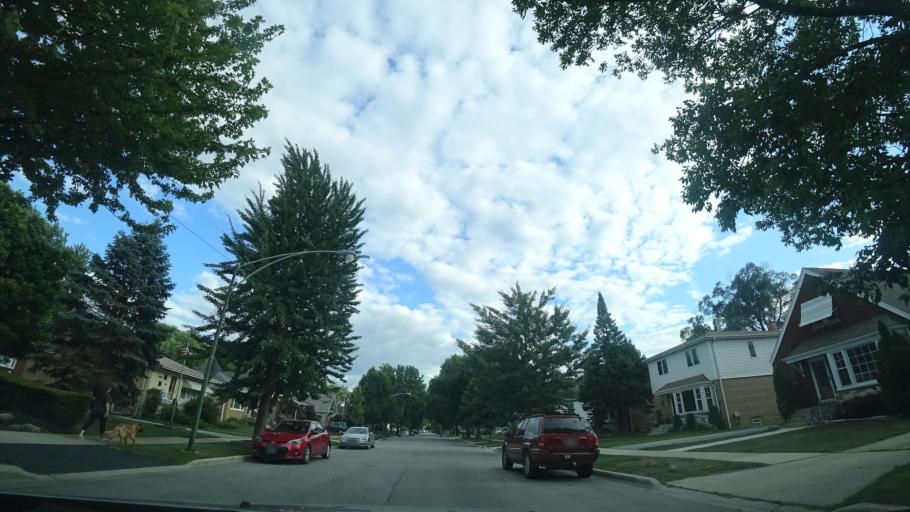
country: US
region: Illinois
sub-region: Cook County
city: Evergreen Park
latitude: 41.7039
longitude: -87.7161
